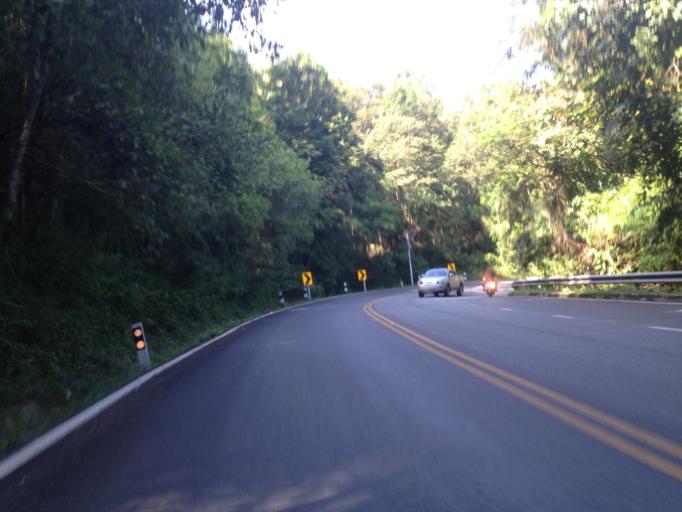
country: TH
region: Chiang Mai
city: Chiang Mai
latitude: 18.8042
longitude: 98.9345
